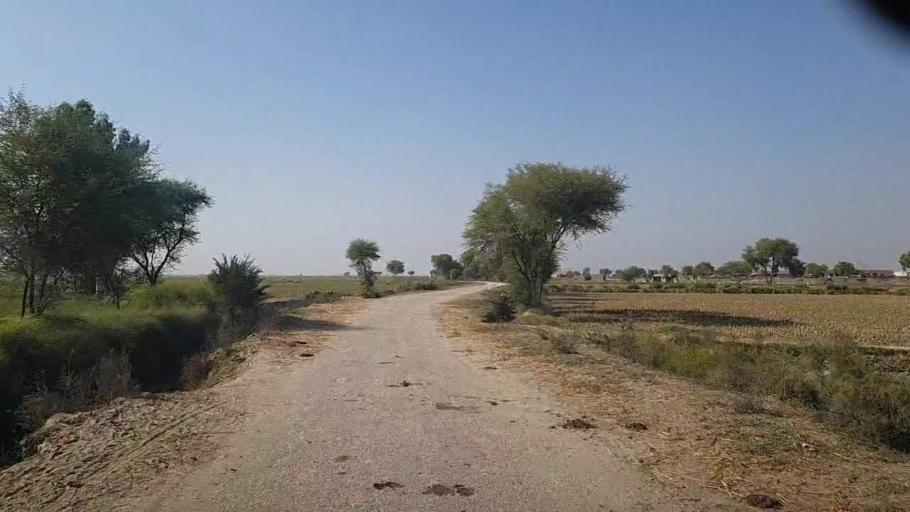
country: PK
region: Sindh
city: Tangwani
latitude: 28.2471
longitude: 68.9463
